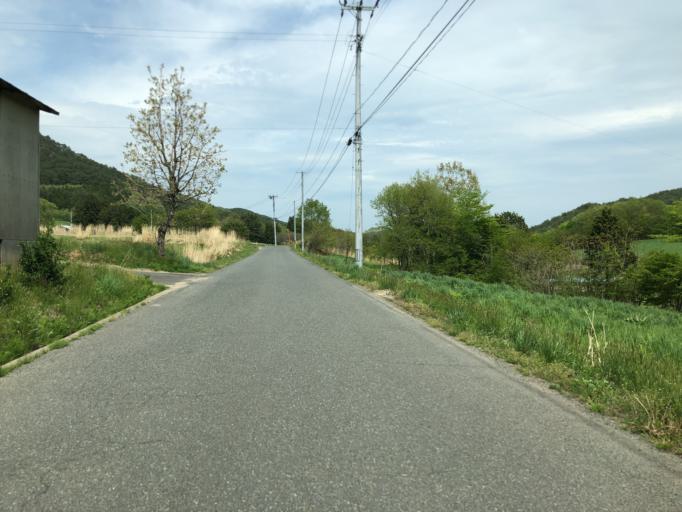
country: JP
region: Fukushima
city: Yanagawamachi-saiwaicho
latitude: 37.7330
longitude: 140.6885
